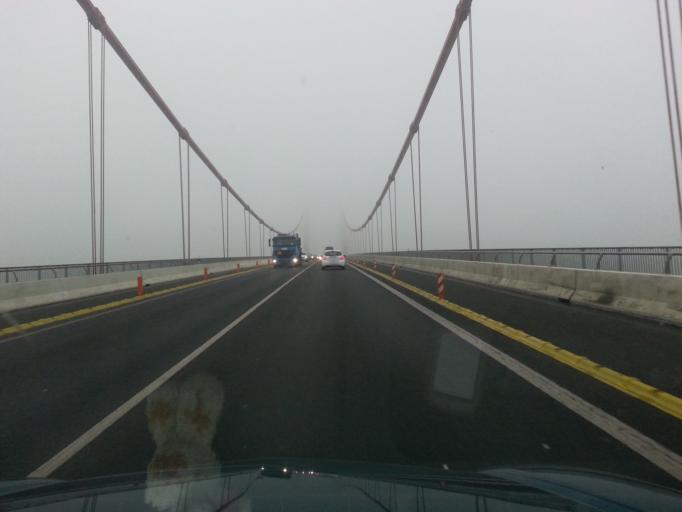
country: DE
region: North Rhine-Westphalia
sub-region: Regierungsbezirk Dusseldorf
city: Emmerich
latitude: 51.8299
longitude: 6.2266
